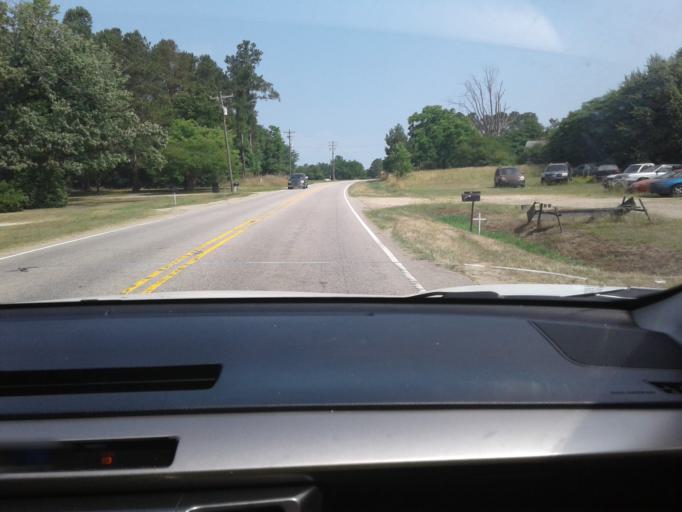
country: US
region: North Carolina
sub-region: Harnett County
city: Coats
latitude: 35.3954
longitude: -78.6717
